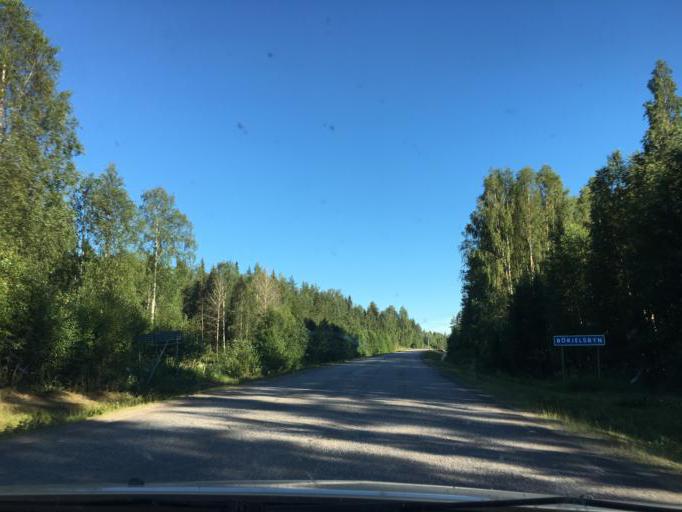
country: SE
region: Norrbotten
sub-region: Kalix Kommun
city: Rolfs
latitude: 65.9134
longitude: 22.9257
